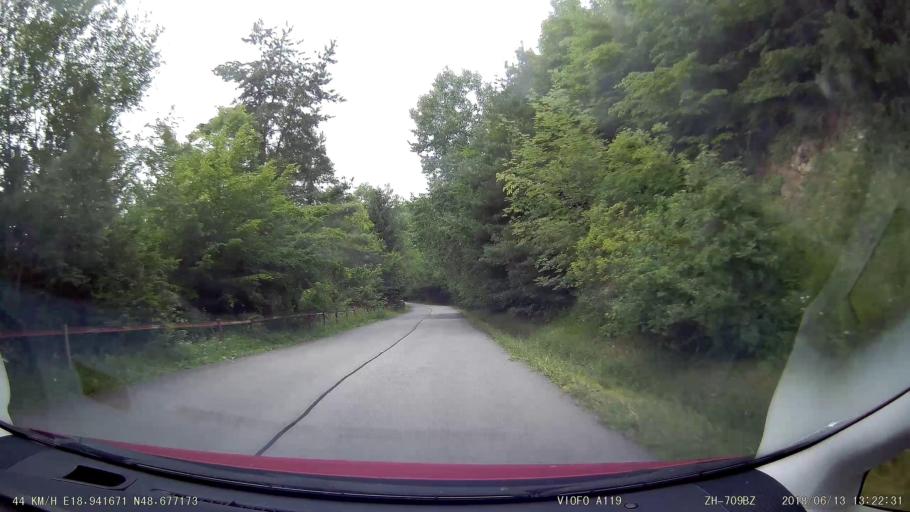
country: SK
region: Banskobystricky
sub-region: Okres Ziar nad Hronom
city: Kremnica
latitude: 48.6771
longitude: 18.9416
